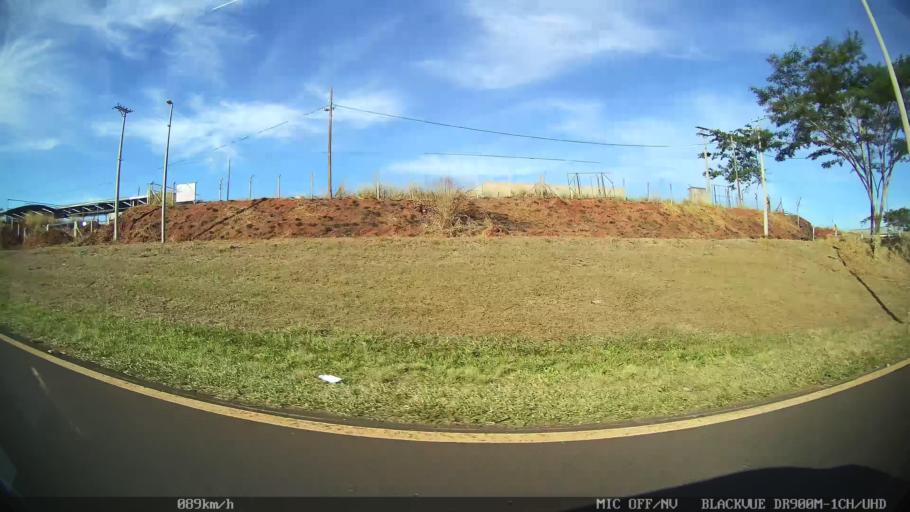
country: BR
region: Sao Paulo
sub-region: Sao Jose Do Rio Preto
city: Sao Jose do Rio Preto
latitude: -20.7388
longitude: -49.3378
